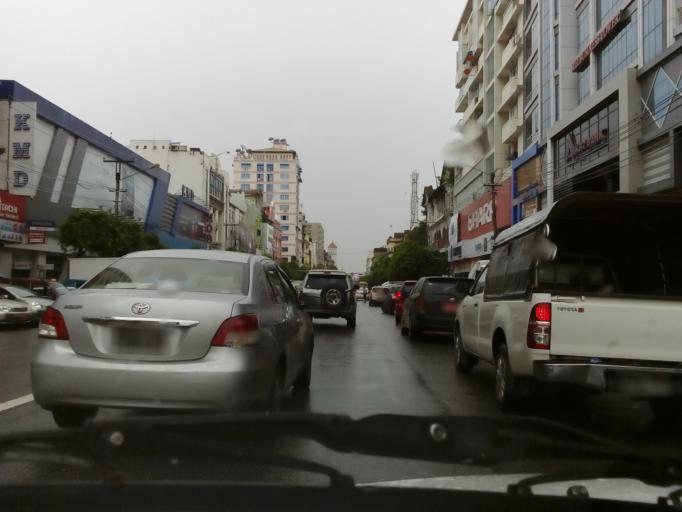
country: MM
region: Yangon
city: Yangon
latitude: 16.7759
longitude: 96.1617
